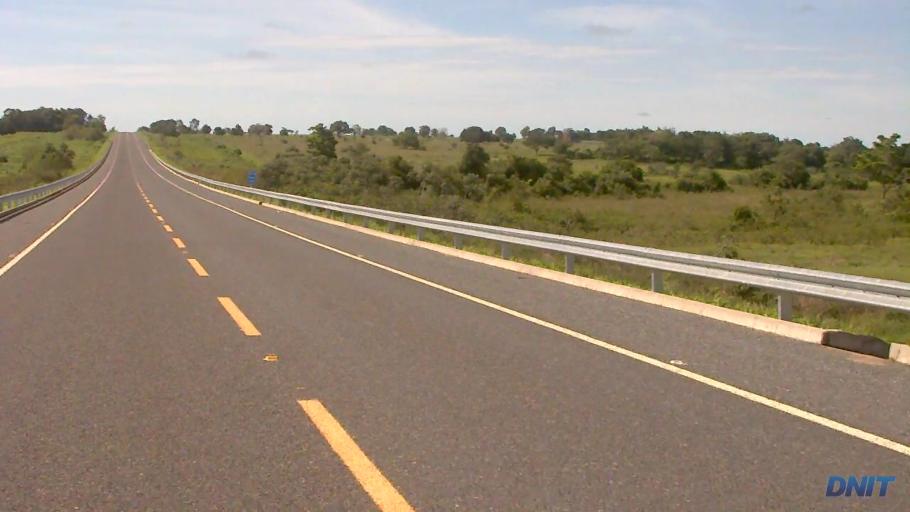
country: BR
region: Goias
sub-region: Sao Miguel Do Araguaia
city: Sao Miguel do Araguaia
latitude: -13.4500
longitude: -50.1208
